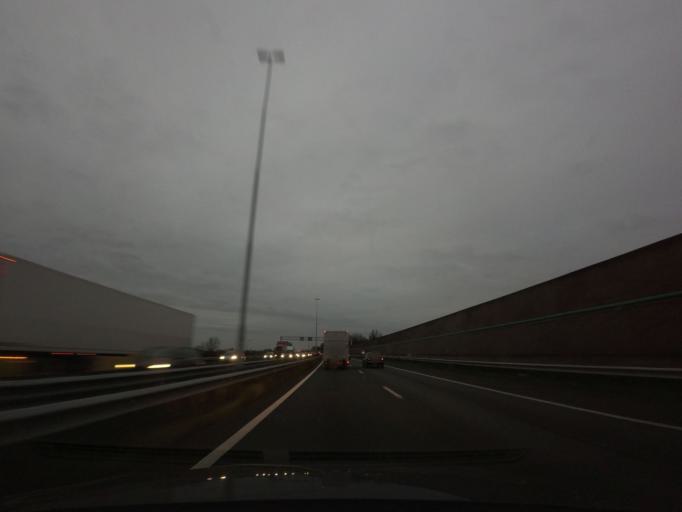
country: NL
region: North Brabant
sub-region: Gemeente Woudrichem
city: Almkerk
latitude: 51.7806
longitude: 4.9273
